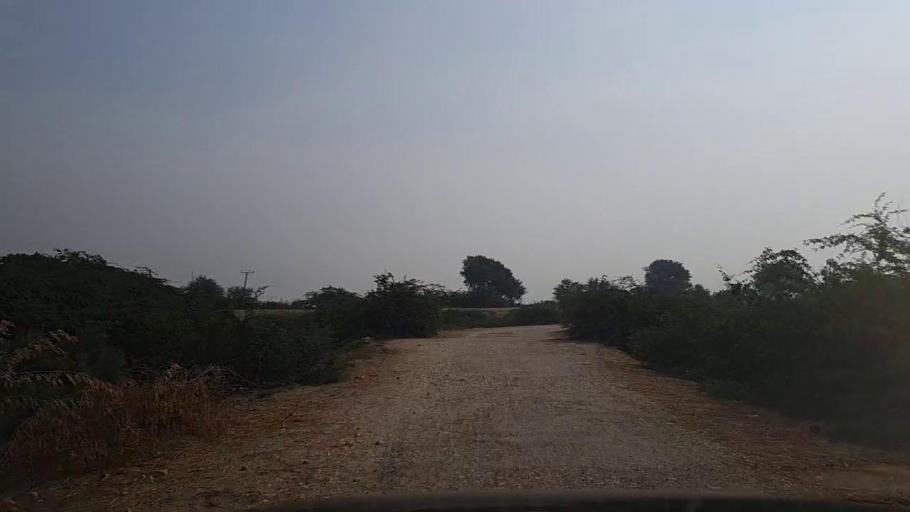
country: PK
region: Sindh
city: Mirpur Sakro
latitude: 24.3762
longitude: 67.7559
